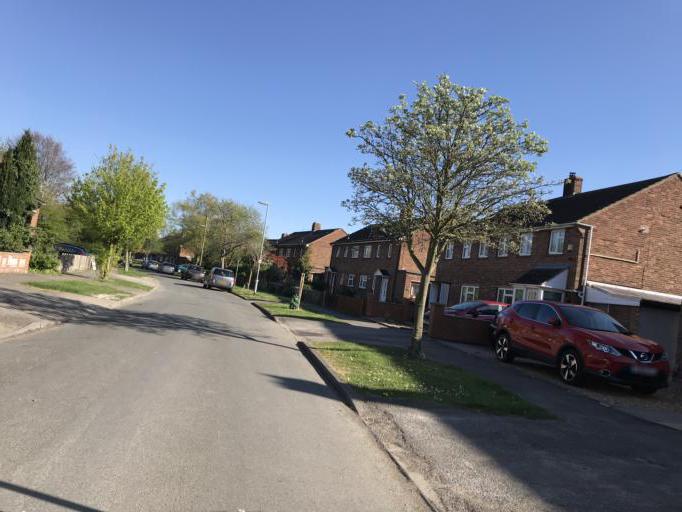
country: GB
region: England
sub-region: Cambridgeshire
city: Cambridge
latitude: 52.2085
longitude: 0.1573
